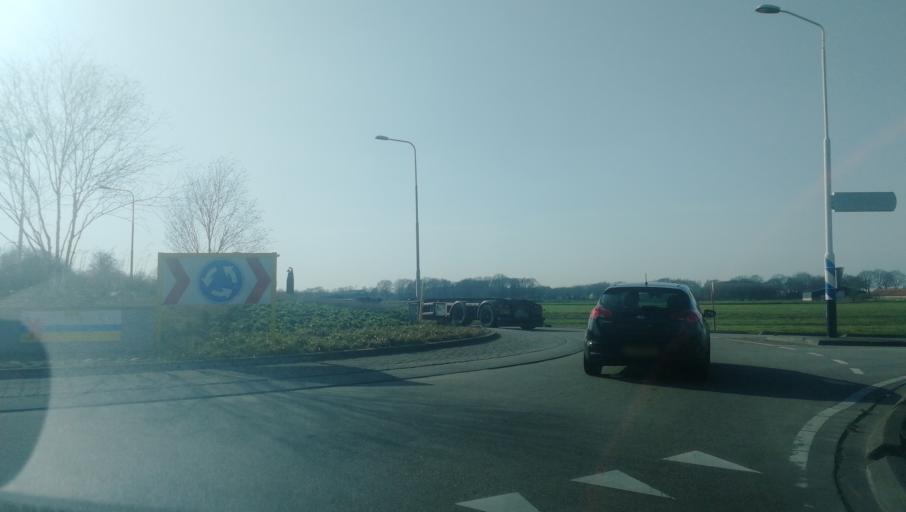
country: NL
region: Limburg
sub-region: Gemeente Peel en Maas
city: Maasbree
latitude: 51.3538
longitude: 6.0310
